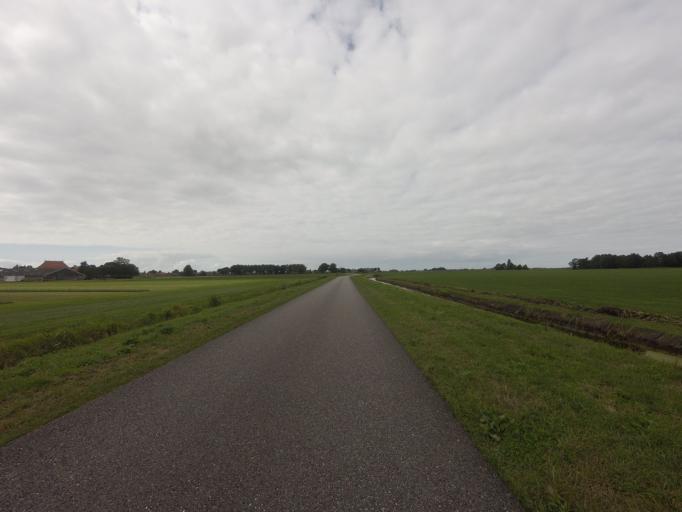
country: NL
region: Friesland
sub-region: Sudwest Fryslan
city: Workum
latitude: 52.9488
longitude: 5.5089
